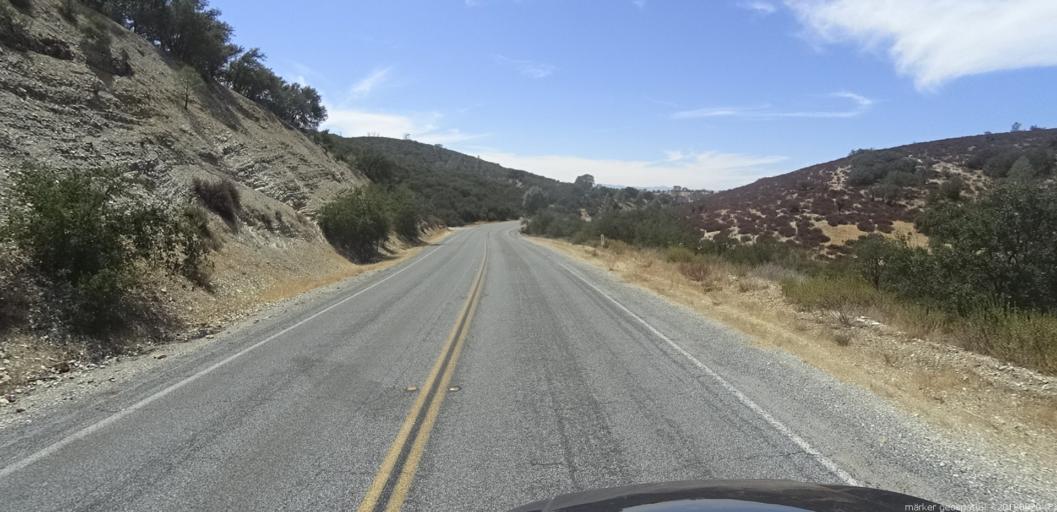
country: US
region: California
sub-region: San Luis Obispo County
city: Lake Nacimiento
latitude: 35.9032
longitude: -120.9713
